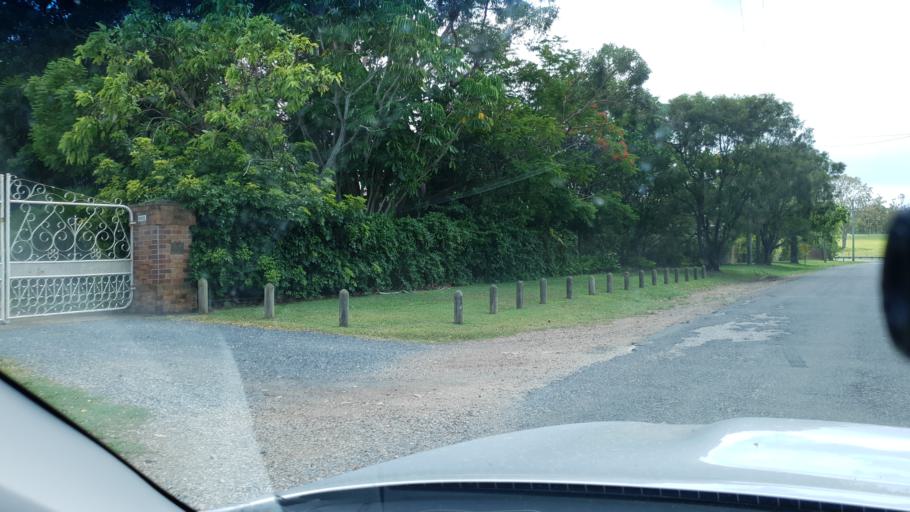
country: AU
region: Queensland
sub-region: Gold Coast
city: Yatala
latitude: -27.6796
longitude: 153.2260
